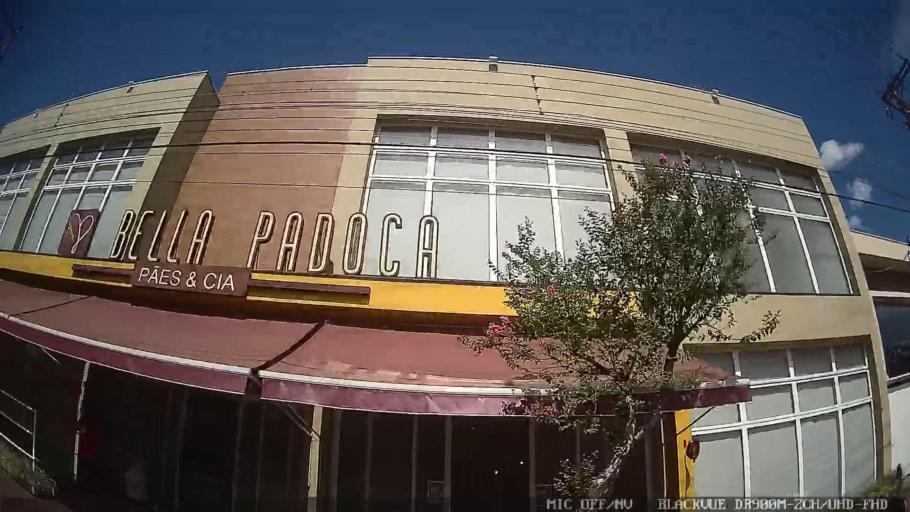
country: BR
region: Sao Paulo
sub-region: Pedreira
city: Pedreira
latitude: -22.7468
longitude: -46.8992
